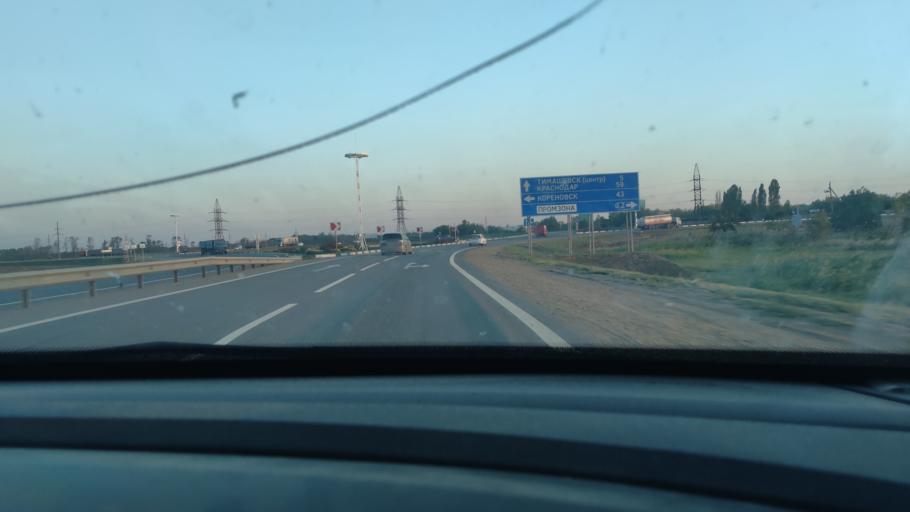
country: RU
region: Krasnodarskiy
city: Timashevsk
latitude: 45.6288
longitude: 38.9839
